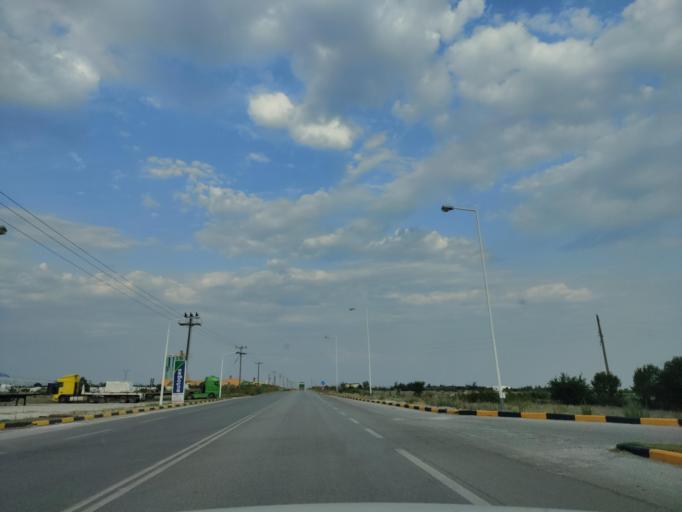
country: GR
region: East Macedonia and Thrace
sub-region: Nomos Dramas
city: Prosotsani
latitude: 41.1800
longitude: 23.9878
